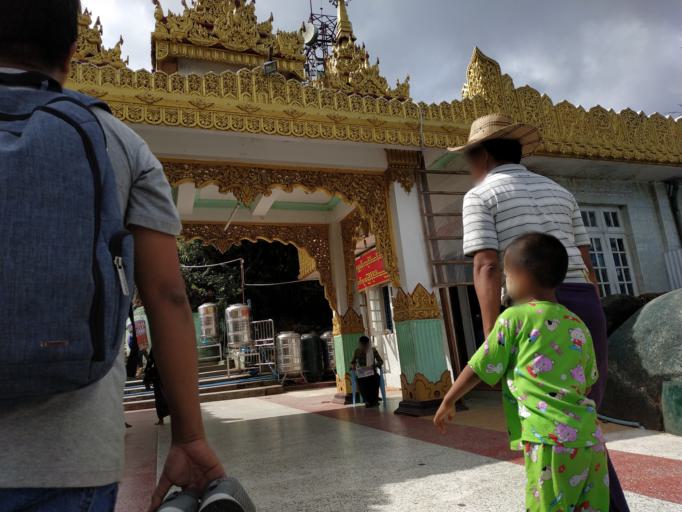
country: MM
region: Mon
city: Kyaikto
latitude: 17.4799
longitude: 97.0998
